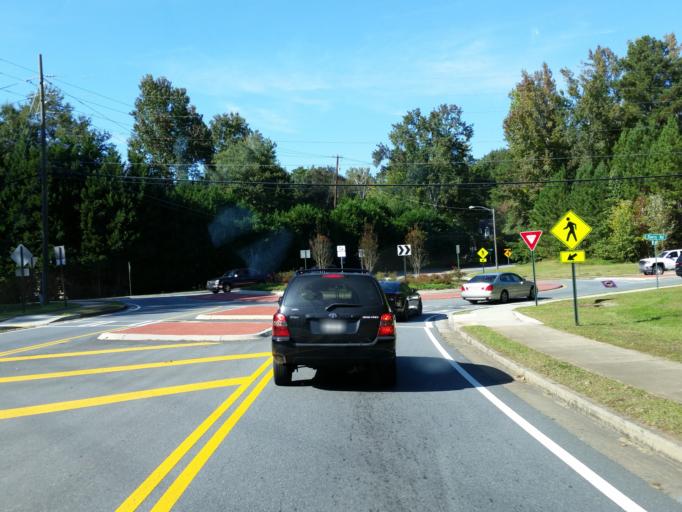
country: US
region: Georgia
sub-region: Cherokee County
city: Woodstock
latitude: 34.0263
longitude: -84.4681
